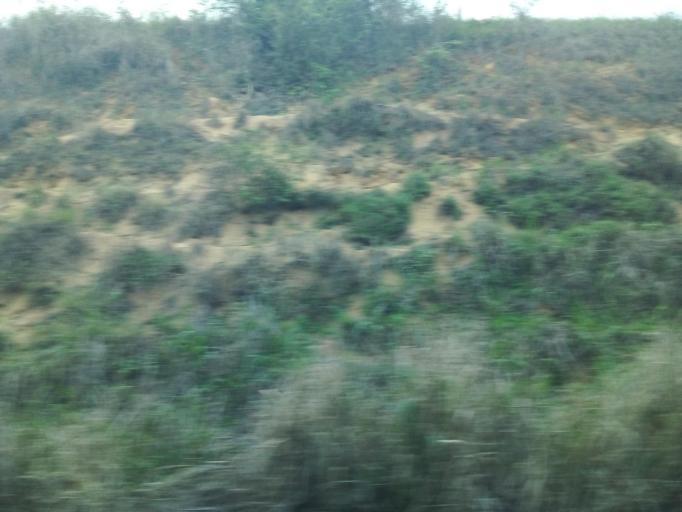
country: BR
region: Minas Gerais
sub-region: Belo Oriente
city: Belo Oriente
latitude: -19.2238
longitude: -42.3002
